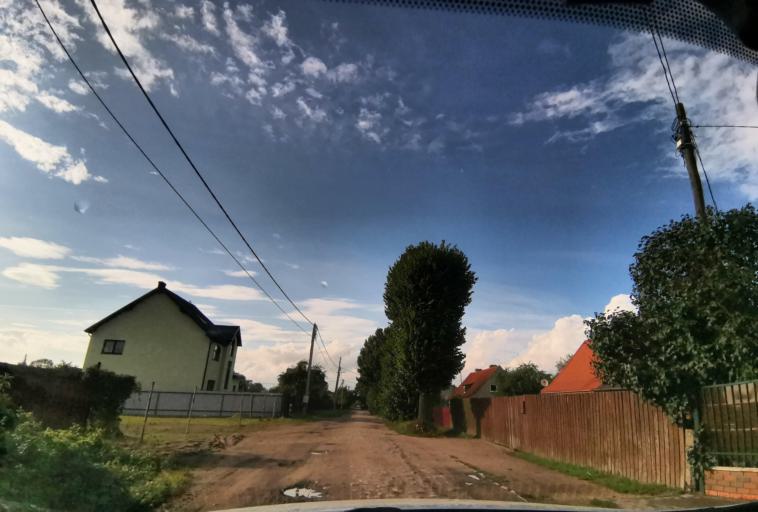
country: RU
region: Kaliningrad
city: Chernyakhovsk
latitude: 54.6562
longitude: 21.8378
